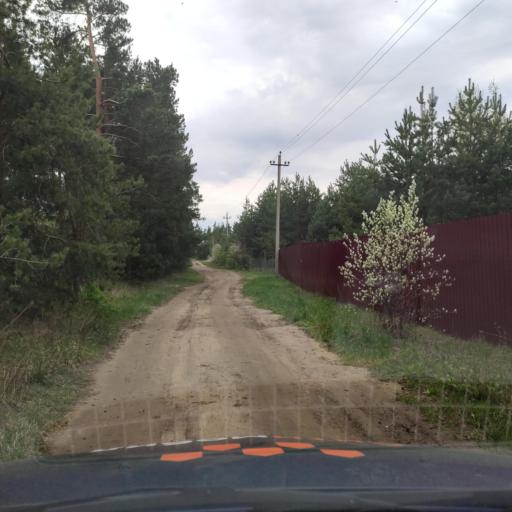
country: RU
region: Voronezj
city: Podgornoye
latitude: 51.8612
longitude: 39.1589
